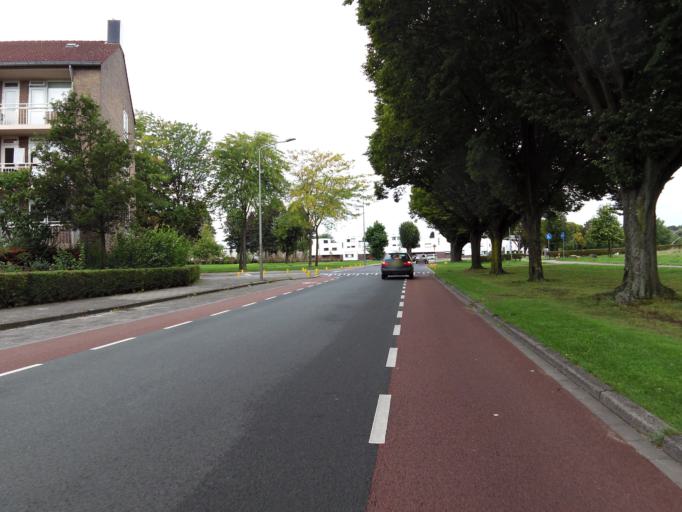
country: NL
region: Limburg
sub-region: Gemeente Heerlen
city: Heerlen
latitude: 50.8963
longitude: 5.9941
